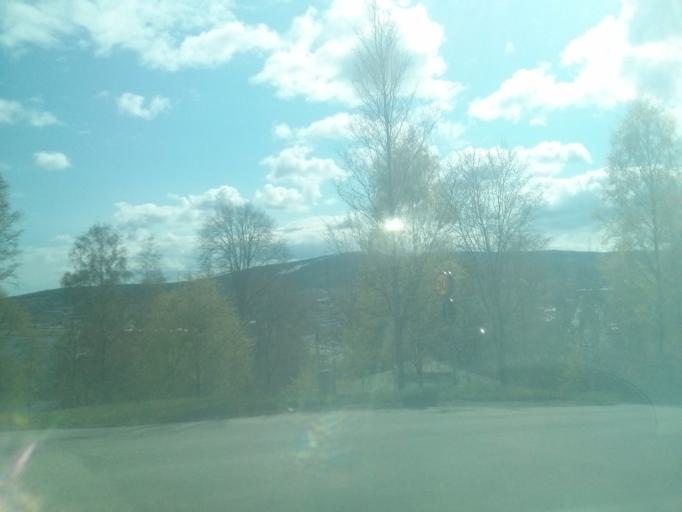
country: SE
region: Vaesternorrland
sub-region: Sundsvalls Kommun
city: Sundsvall
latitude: 62.3977
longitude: 17.3119
